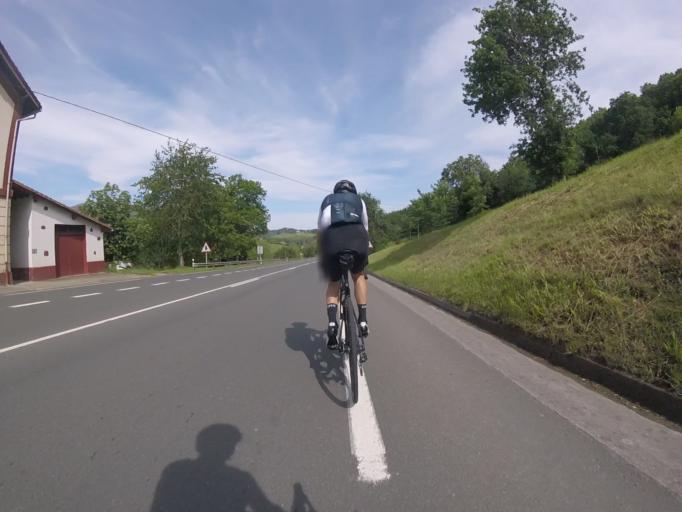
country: ES
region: Basque Country
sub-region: Provincia de Guipuzcoa
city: Cestona
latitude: 43.2572
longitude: -2.2688
